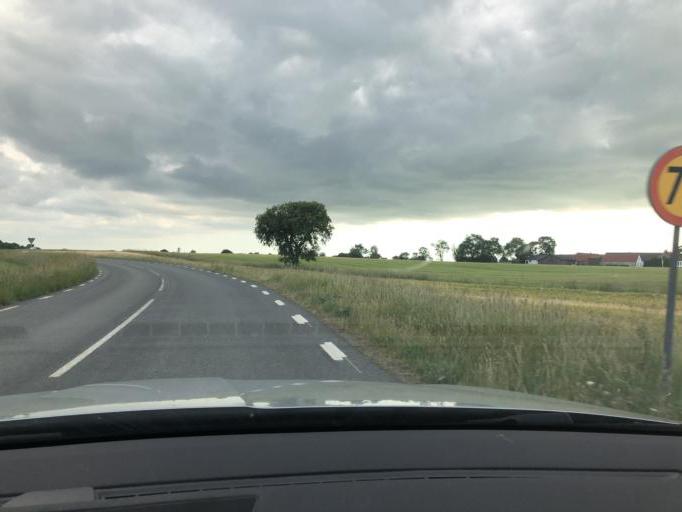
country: SE
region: Skane
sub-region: Simrishamns Kommun
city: Simrishamn
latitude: 55.5269
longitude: 14.2386
